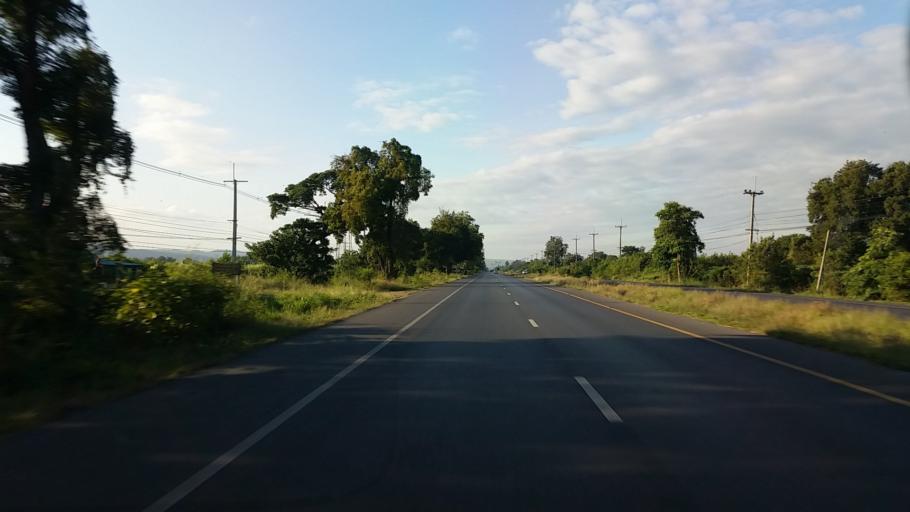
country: TH
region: Lop Buri
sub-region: Amphoe Tha Luang
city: Tha Luang
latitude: 15.0376
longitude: 100.9549
